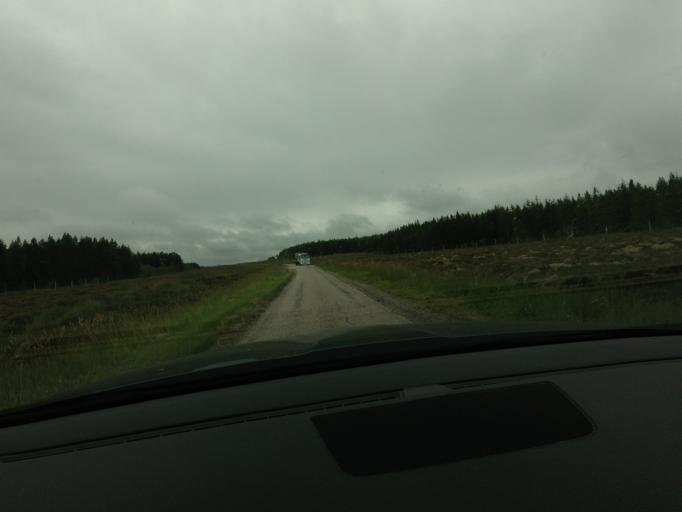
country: GB
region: Scotland
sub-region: Highland
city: Evanton
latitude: 58.1933
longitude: -4.5146
